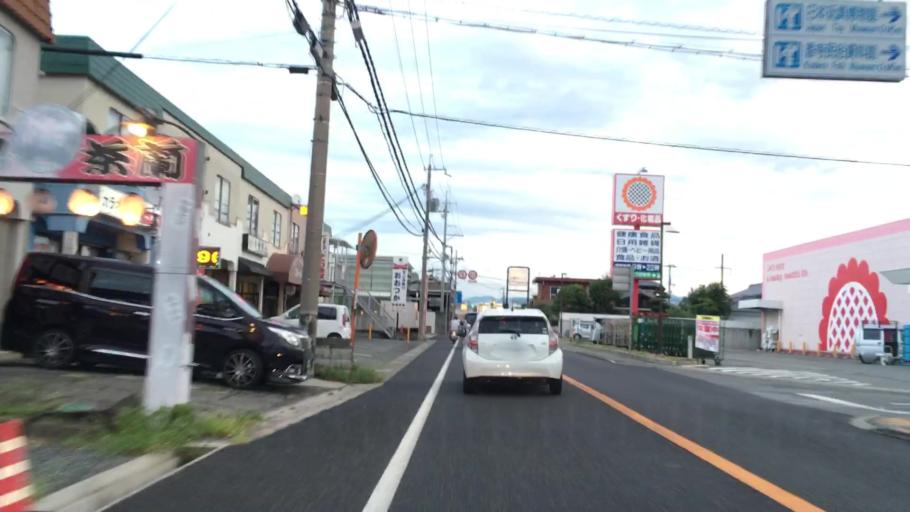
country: JP
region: Hyogo
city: Himeji
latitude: 34.9087
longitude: 134.7383
